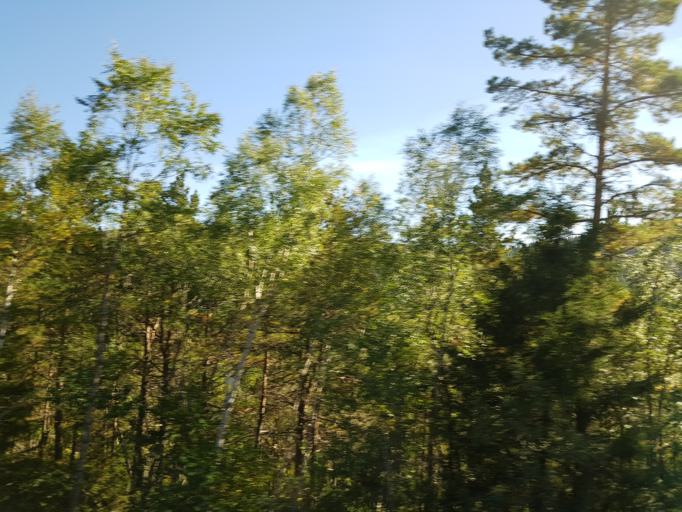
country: NO
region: Sor-Trondelag
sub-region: Afjord
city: A i Afjord
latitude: 63.7836
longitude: 10.2239
